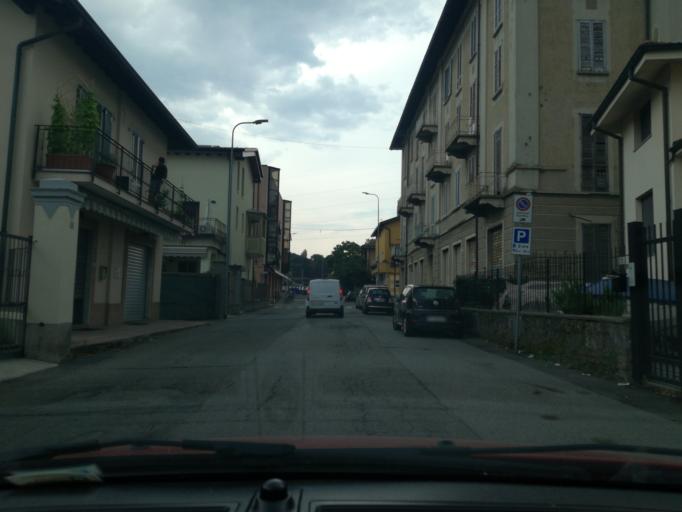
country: IT
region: Lombardy
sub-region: Provincia di Monza e Brianza
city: Carnate
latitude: 45.6522
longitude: 9.3720
